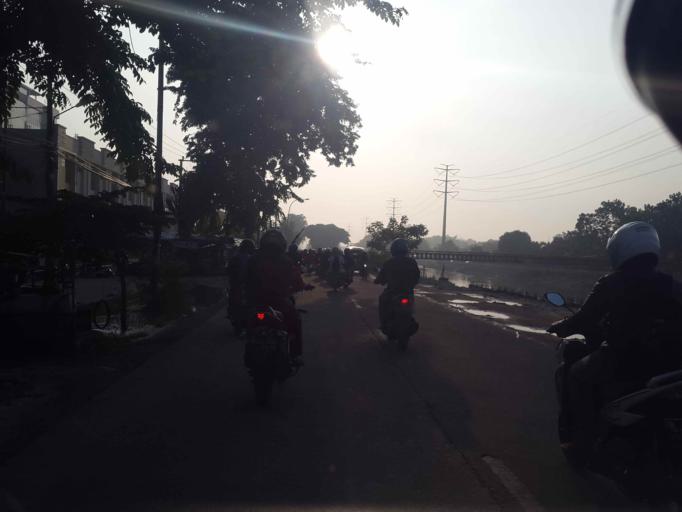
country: ID
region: West Java
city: Bekasi
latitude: -6.2639
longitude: 107.0265
